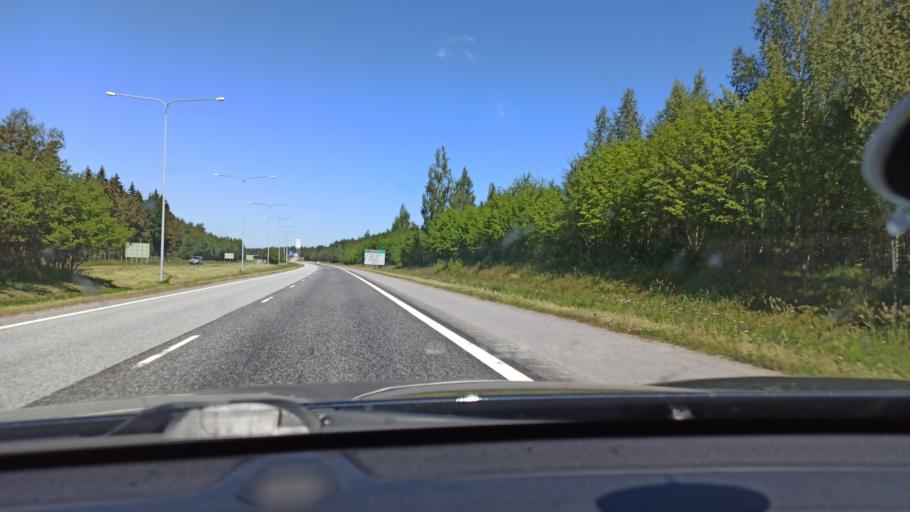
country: FI
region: Ostrobothnia
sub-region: Vaasa
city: Ristinummi
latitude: 63.0622
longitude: 21.7081
